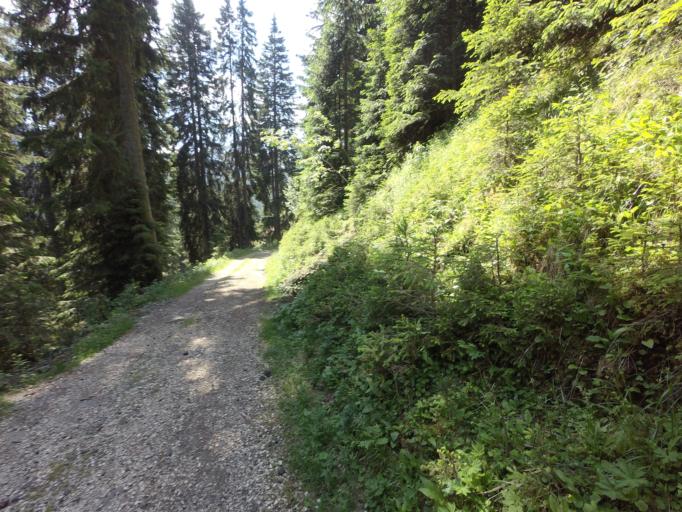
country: IT
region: Trentino-Alto Adige
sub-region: Bolzano
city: Ortisei
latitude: 46.5190
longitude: 11.6637
